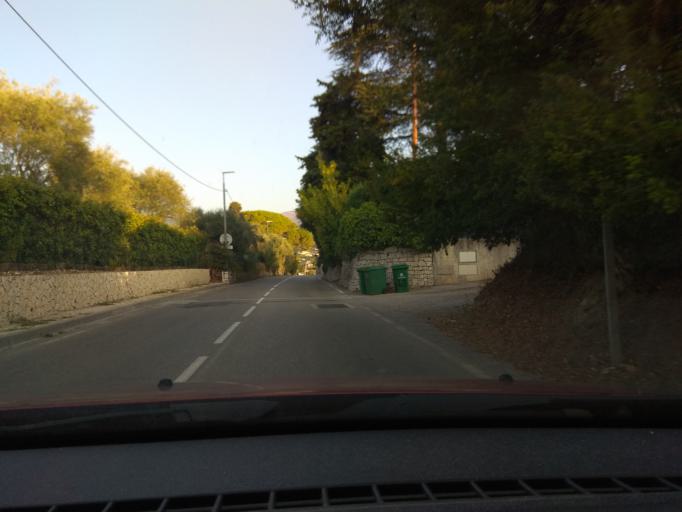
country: FR
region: Provence-Alpes-Cote d'Azur
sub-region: Departement des Alpes-Maritimes
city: La Colle-sur-Loup
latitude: 43.6814
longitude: 7.1140
